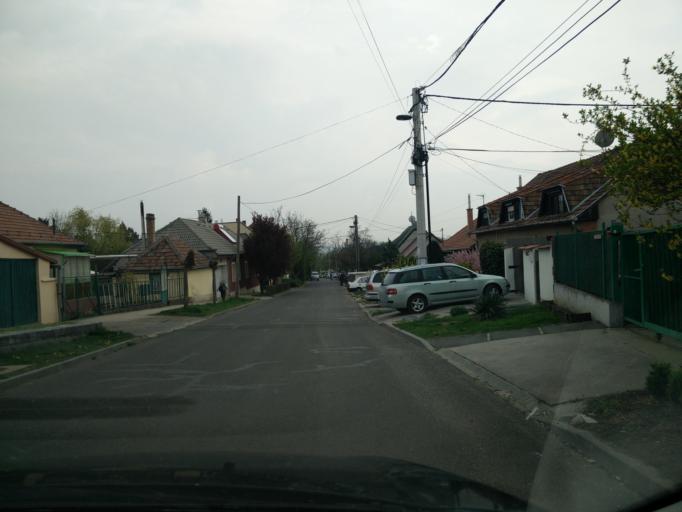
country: HU
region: Pest
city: Budaors
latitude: 47.4651
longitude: 18.9608
